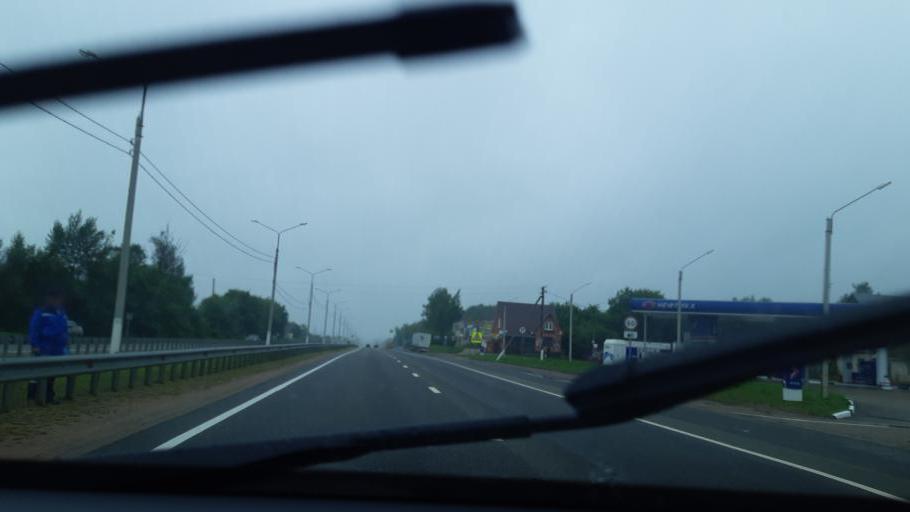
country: RU
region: Smolensk
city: Talashkino
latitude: 54.6476
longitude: 32.1709
